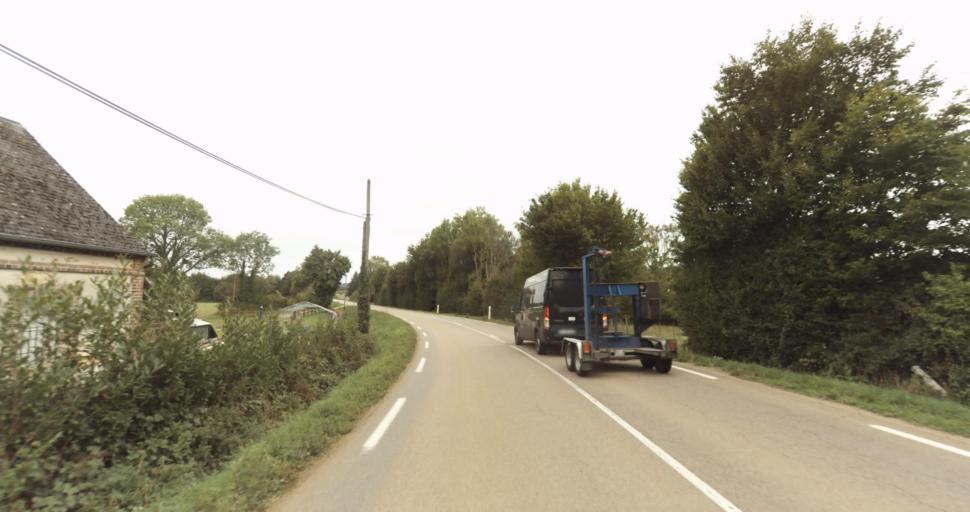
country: FR
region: Lower Normandy
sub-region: Departement de l'Orne
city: Gace
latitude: 48.7648
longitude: 0.3337
